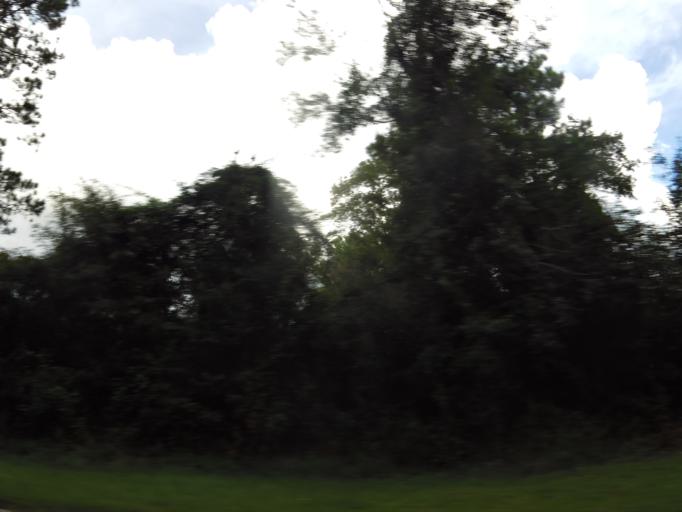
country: US
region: Georgia
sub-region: Liberty County
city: Midway
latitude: 31.8594
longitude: -81.4300
